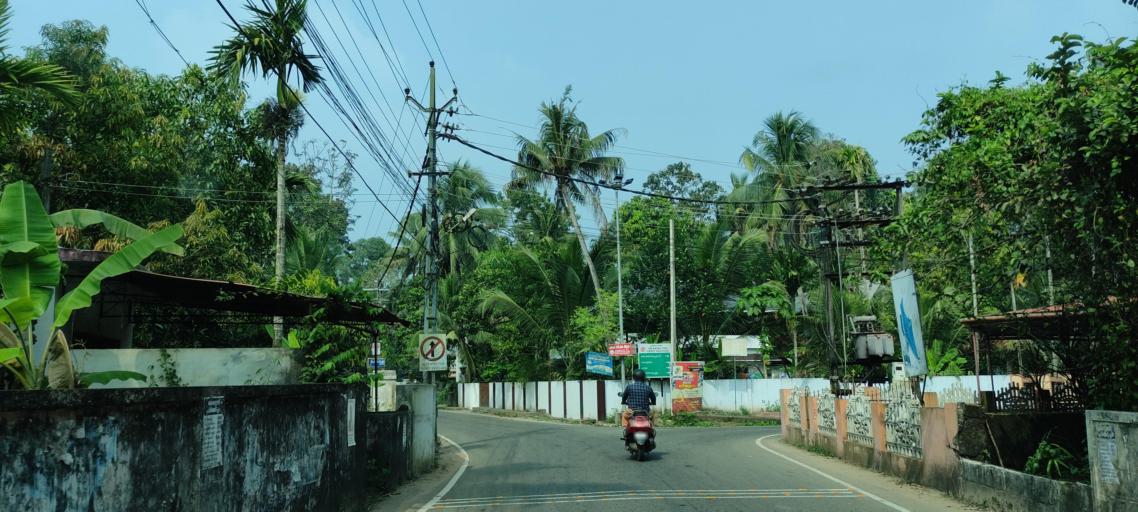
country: IN
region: Kerala
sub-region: Kottayam
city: Vaikam
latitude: 9.7453
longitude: 76.4019
